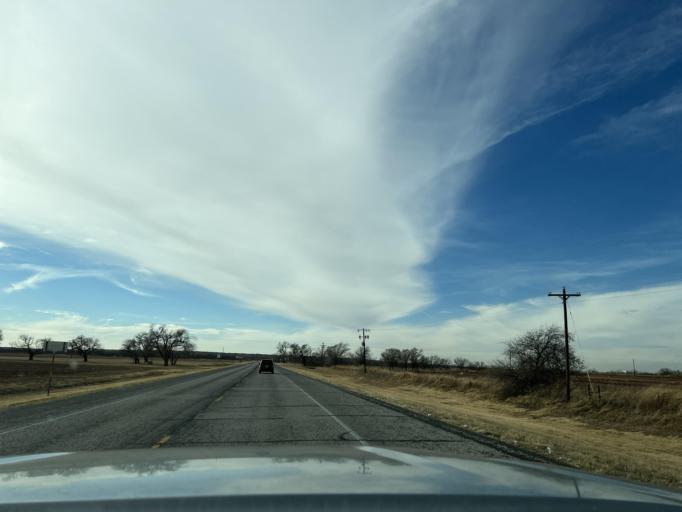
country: US
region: Texas
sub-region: Fisher County
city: Roby
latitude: 32.7612
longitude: -100.2992
